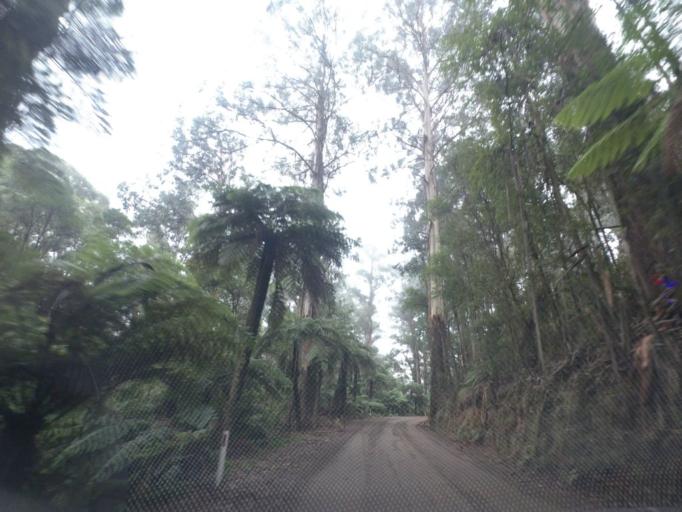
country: AU
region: Victoria
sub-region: Yarra Ranges
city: Launching Place
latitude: -37.7148
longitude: 145.5905
